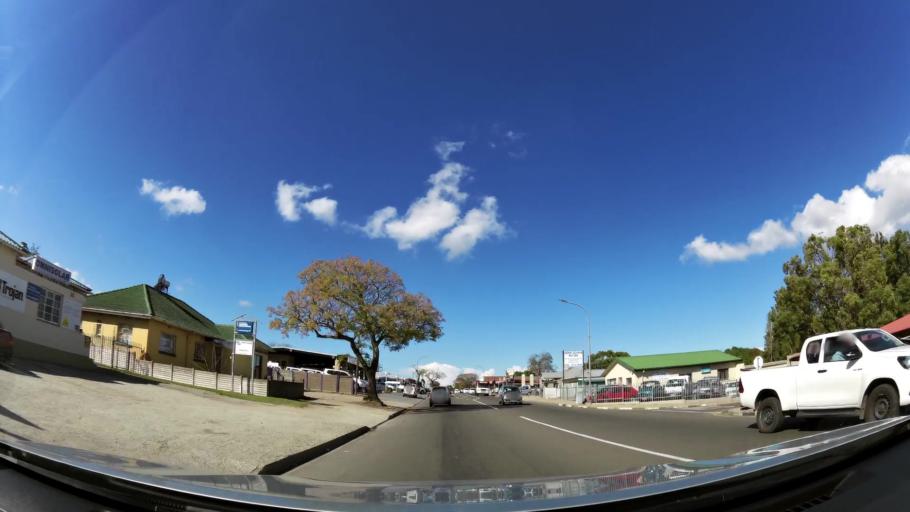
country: ZA
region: Western Cape
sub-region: Eden District Municipality
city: George
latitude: -33.9670
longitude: 22.4589
